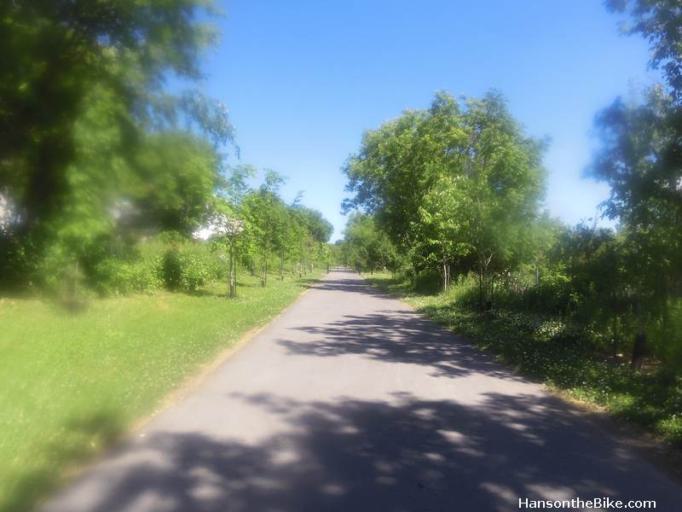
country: CA
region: Ontario
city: Kingston
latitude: 44.2451
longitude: -76.4841
